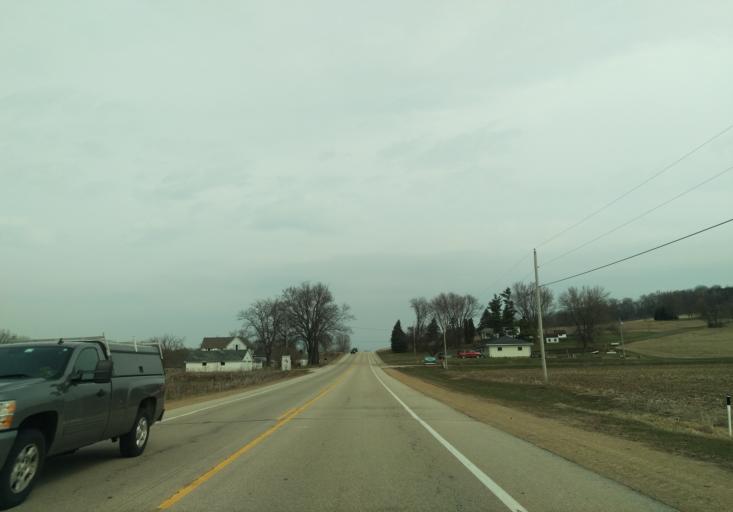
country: US
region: Wisconsin
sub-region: Columbia County
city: Lodi
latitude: 43.3000
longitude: -89.5239
